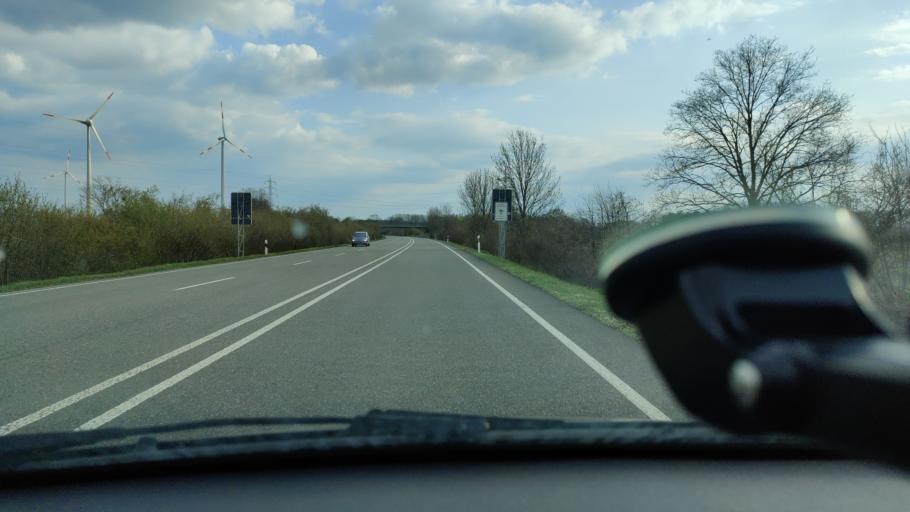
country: DE
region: North Rhine-Westphalia
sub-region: Regierungsbezirk Dusseldorf
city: Bocholt
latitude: 51.7949
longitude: 6.5777
